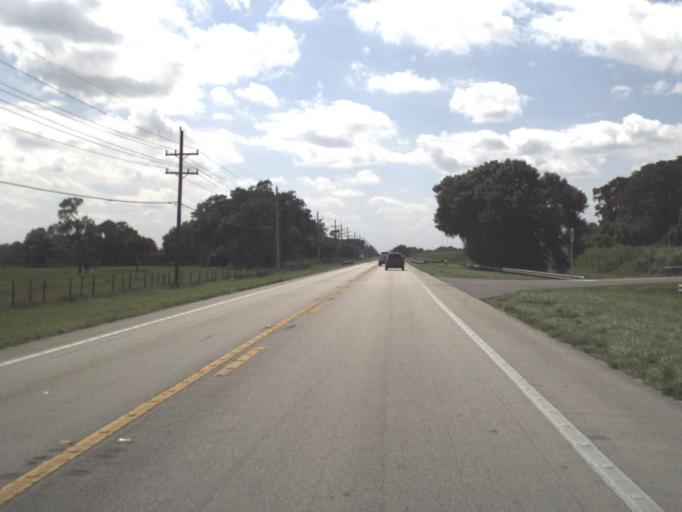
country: US
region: Florida
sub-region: Hendry County
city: LaBelle
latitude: 26.7227
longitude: -81.4376
